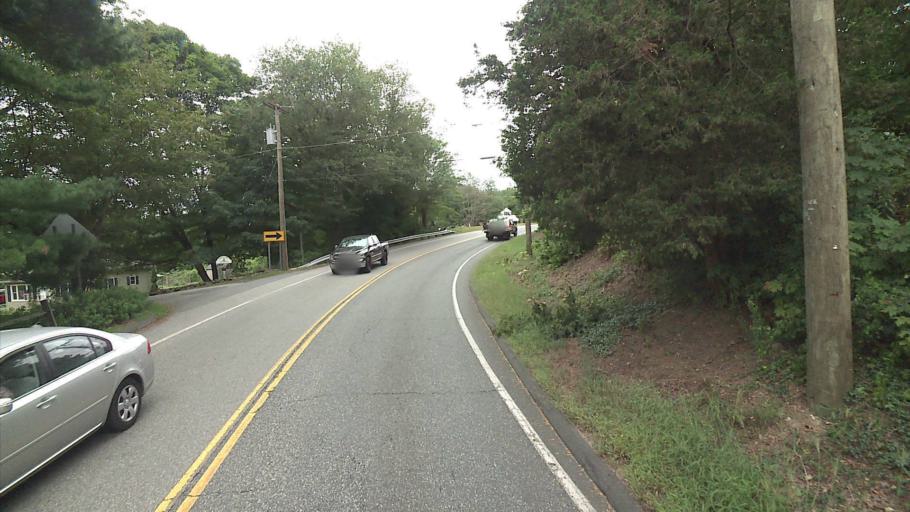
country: US
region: Connecticut
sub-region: New London County
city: Niantic
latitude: 41.3080
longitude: -72.2559
